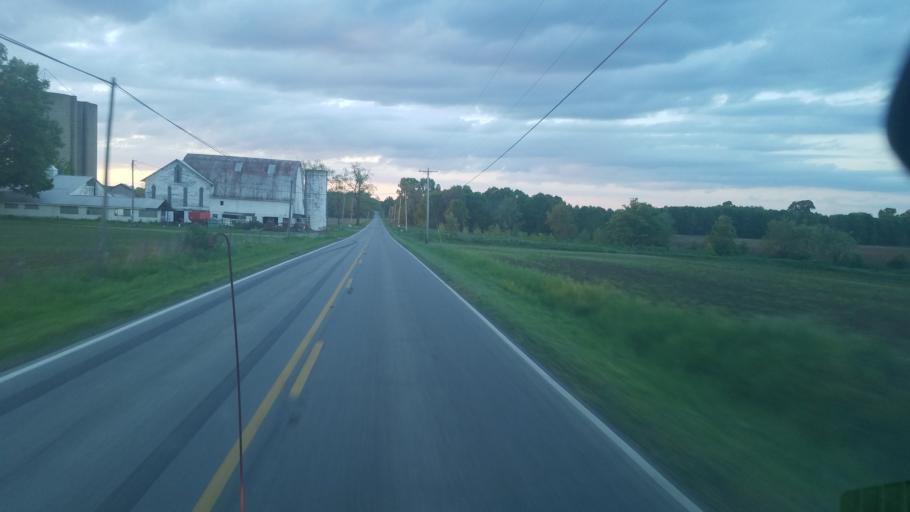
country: US
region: Ohio
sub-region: Wayne County
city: Apple Creek
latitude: 40.7492
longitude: -81.8959
